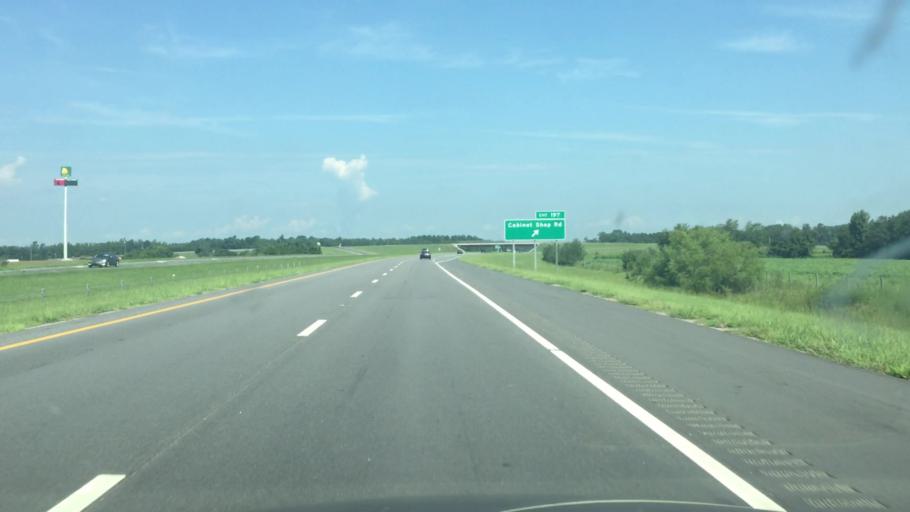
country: US
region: North Carolina
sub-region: Robeson County
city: Pembroke
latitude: 34.6762
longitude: -79.2706
